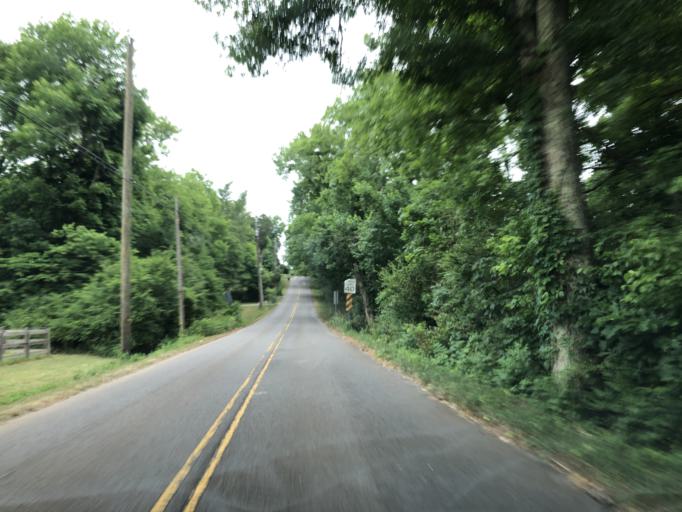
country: US
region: Tennessee
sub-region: Davidson County
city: Goodlettsville
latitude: 36.2871
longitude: -86.7661
